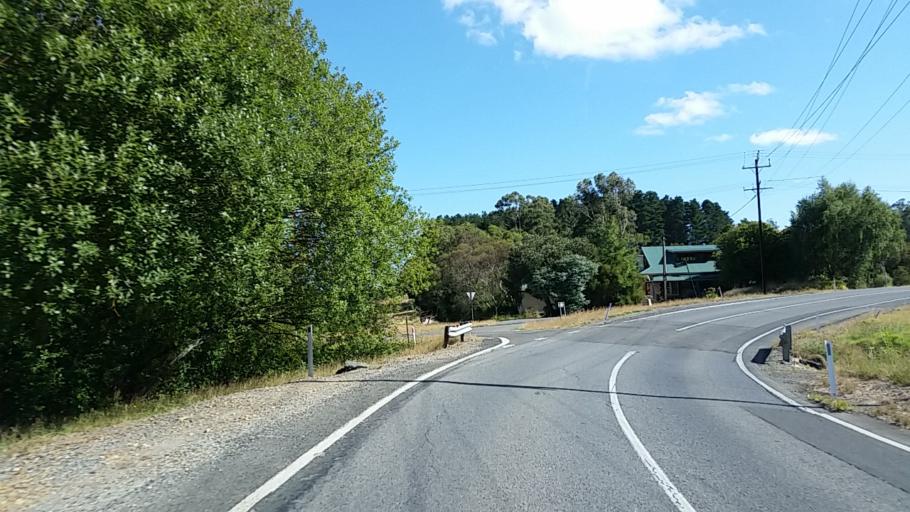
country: AU
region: South Australia
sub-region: Adelaide Hills
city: Bridgewater
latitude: -34.9715
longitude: 138.7330
